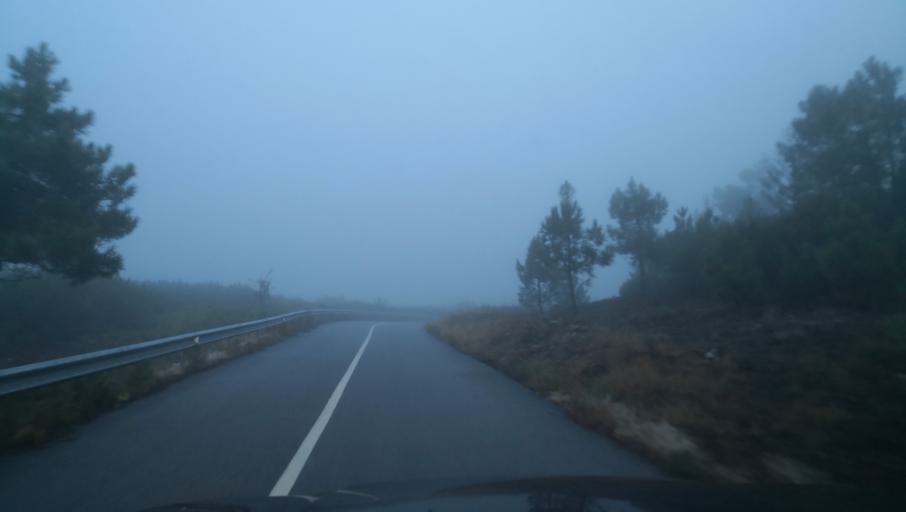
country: PT
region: Vila Real
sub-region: Sabrosa
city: Sabrosa
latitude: 41.2850
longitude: -7.5988
